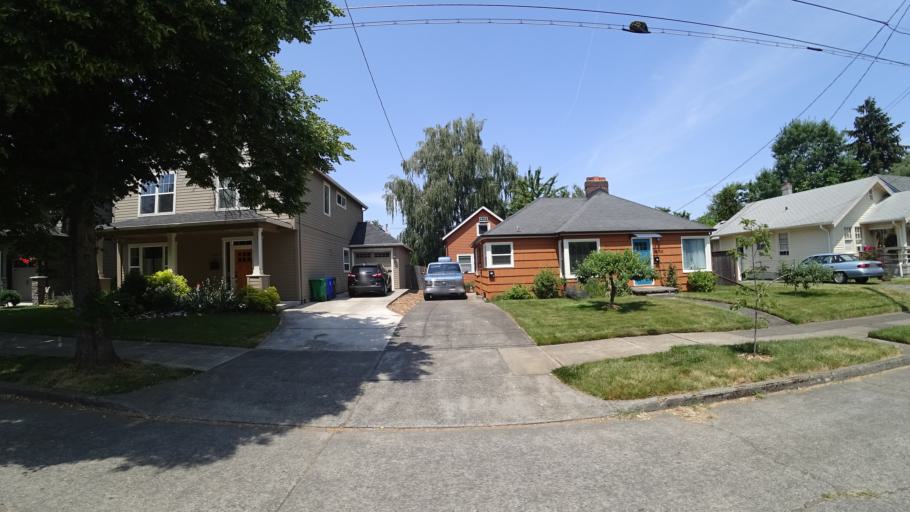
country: US
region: Oregon
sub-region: Multnomah County
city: Portland
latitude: 45.5820
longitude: -122.6938
